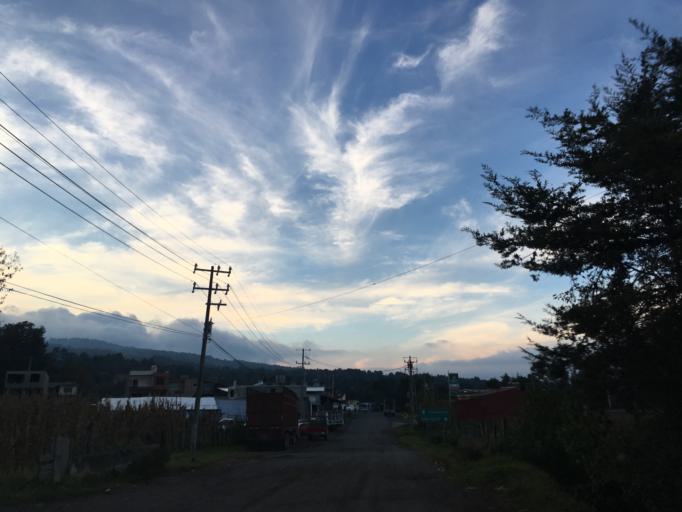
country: MX
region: Michoacan
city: Charapan
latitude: 19.6137
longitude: -102.2342
